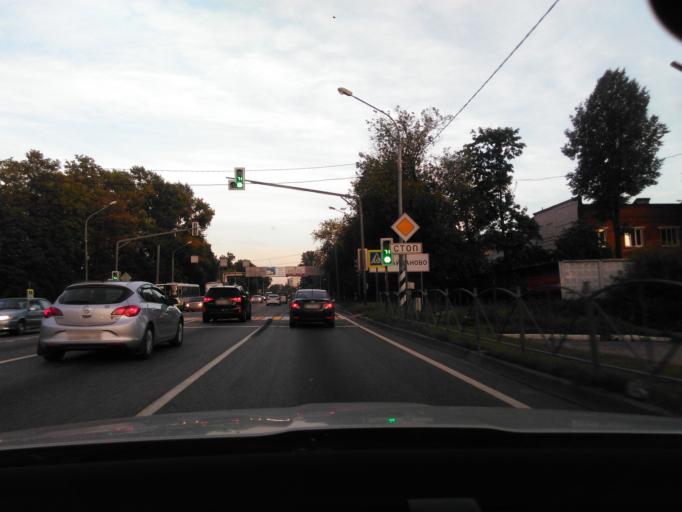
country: RU
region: Moskovskaya
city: Klin
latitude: 56.3436
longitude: 36.7108
